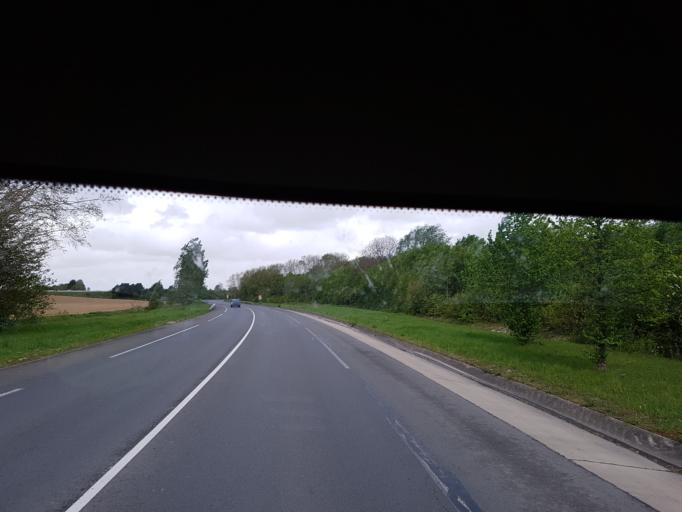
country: FR
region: Nord-Pas-de-Calais
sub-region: Departement du Nord
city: Proville
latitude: 50.1787
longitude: 3.1939
